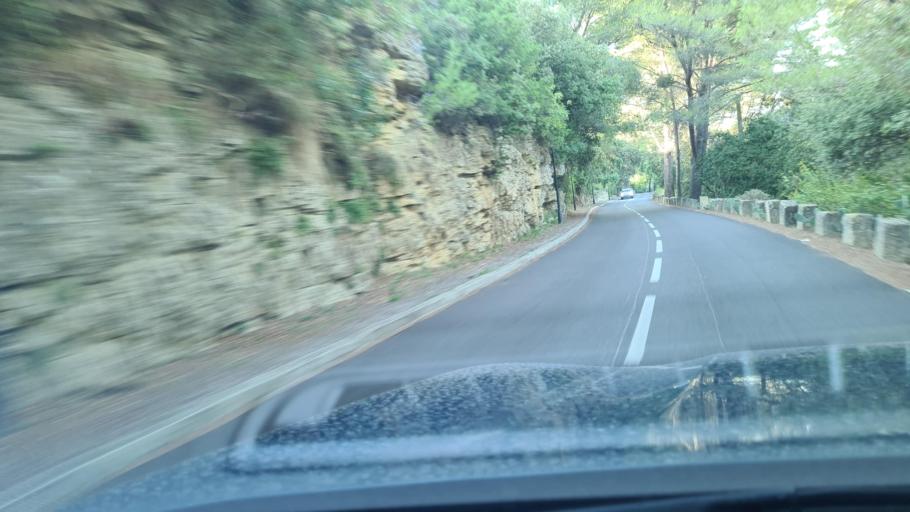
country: FR
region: Provence-Alpes-Cote d'Azur
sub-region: Departement des Bouches-du-Rhone
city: Cornillon-Confoux
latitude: 43.5667
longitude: 5.0727
